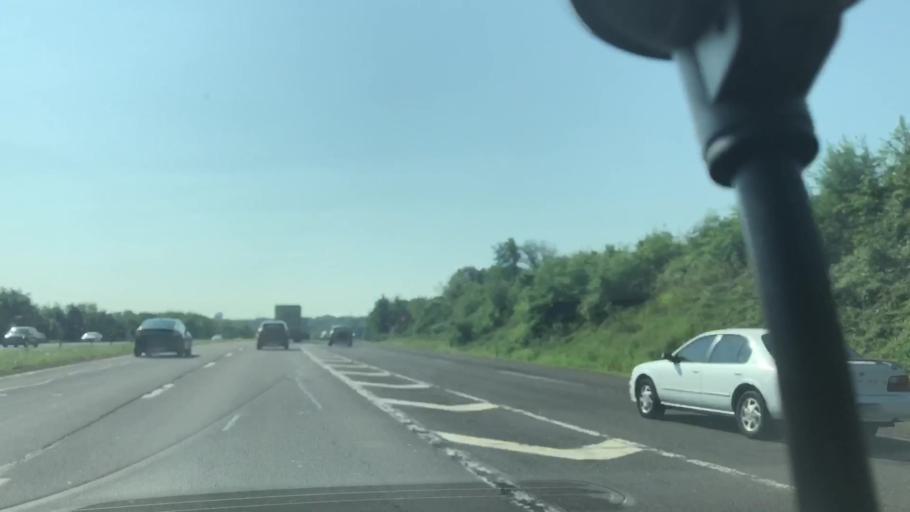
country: US
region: Pennsylvania
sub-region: Montgomery County
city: Royersford
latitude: 40.1935
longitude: -75.5227
